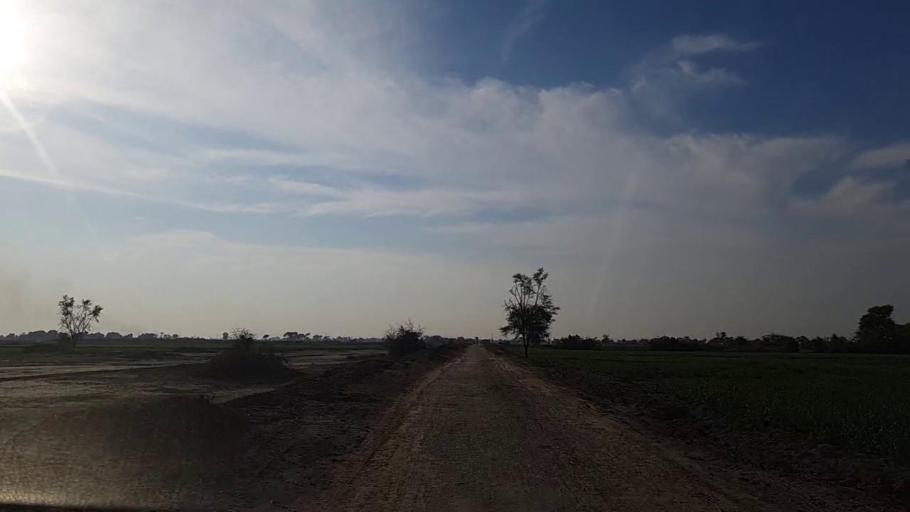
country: PK
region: Sindh
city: Bandhi
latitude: 26.5532
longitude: 68.2569
